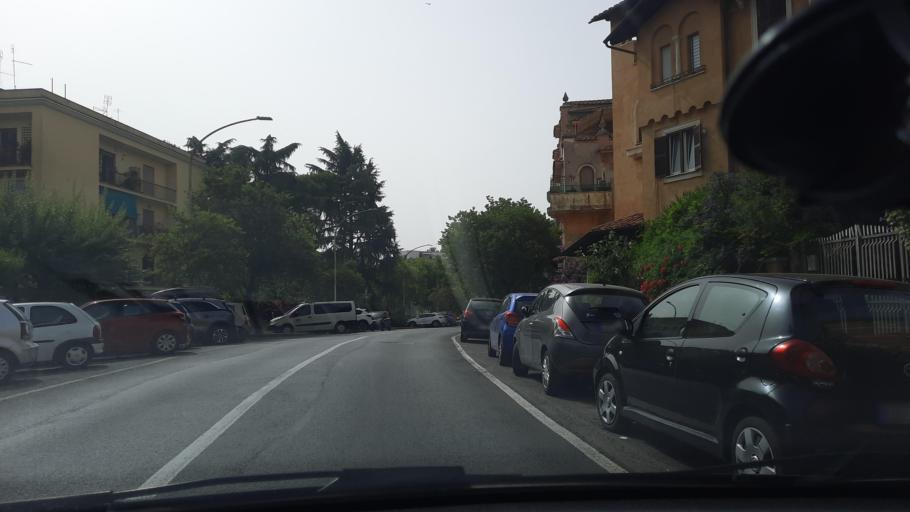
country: IT
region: Latium
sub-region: Citta metropolitana di Roma Capitale
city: Rome
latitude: 41.8596
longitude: 12.4886
